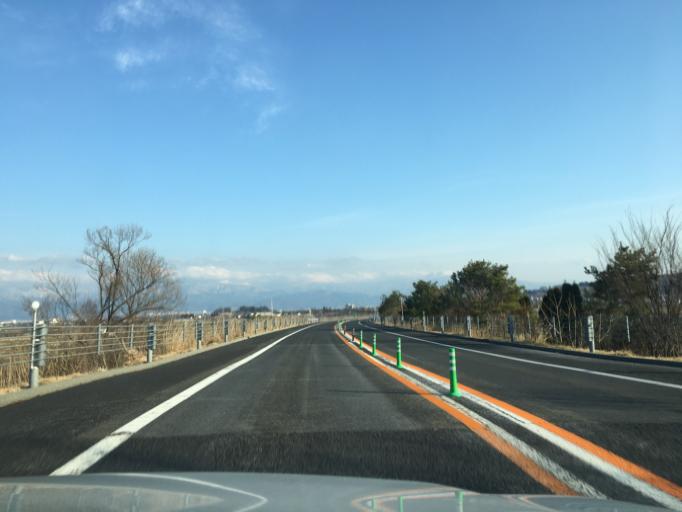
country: JP
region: Yamagata
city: Sagae
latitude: 38.3783
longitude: 140.2412
